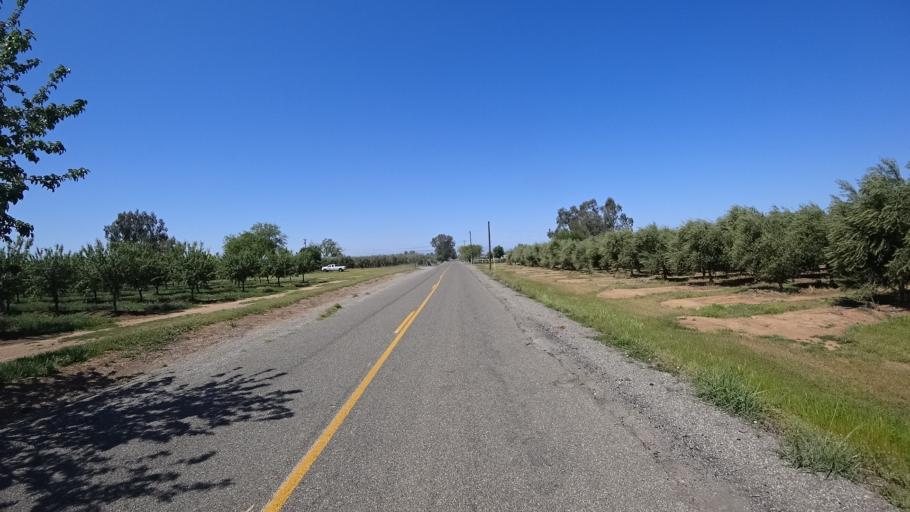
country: US
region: California
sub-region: Glenn County
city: Orland
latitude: 39.7871
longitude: -122.1769
